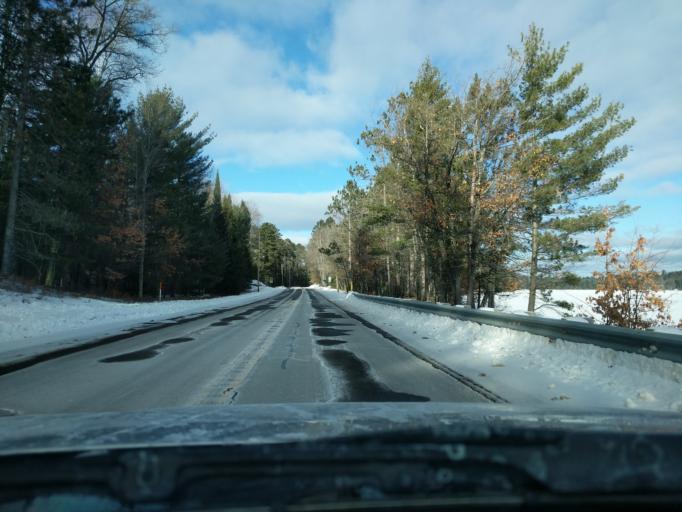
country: US
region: Wisconsin
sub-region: Vilas County
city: Eagle River
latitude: 45.7762
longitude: -89.0754
